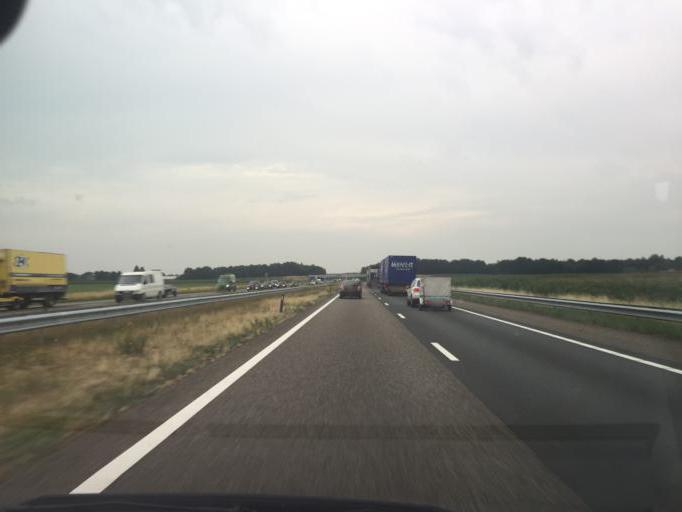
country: NL
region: Limburg
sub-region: Gemeente Leudal
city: Heythuysen
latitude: 51.3826
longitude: 5.8944
